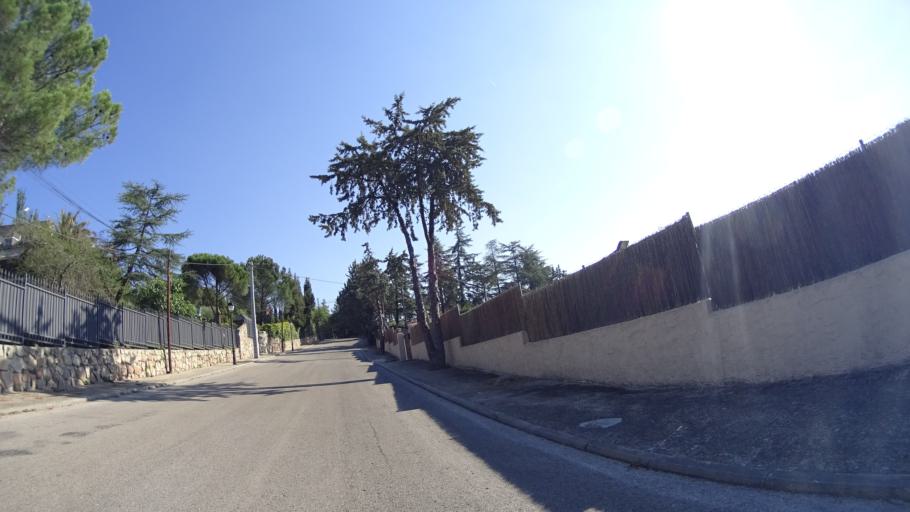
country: ES
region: Madrid
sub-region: Provincia de Madrid
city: Las Matas
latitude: 40.5740
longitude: -3.9016
